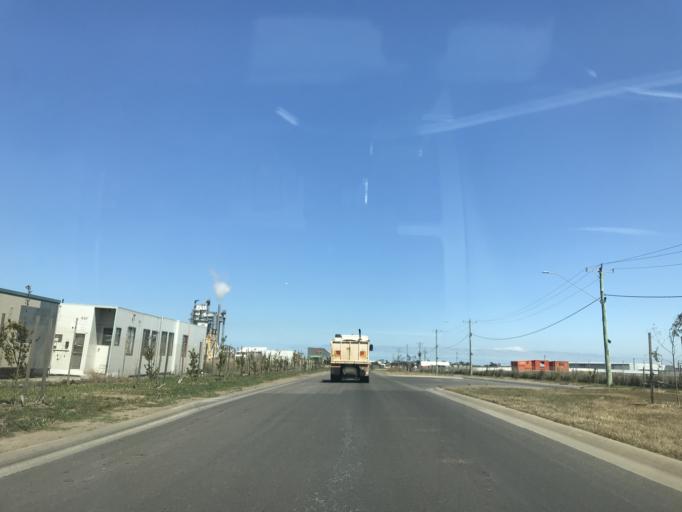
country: AU
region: Victoria
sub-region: Wyndham
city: Truganina
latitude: -37.8279
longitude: 144.7704
